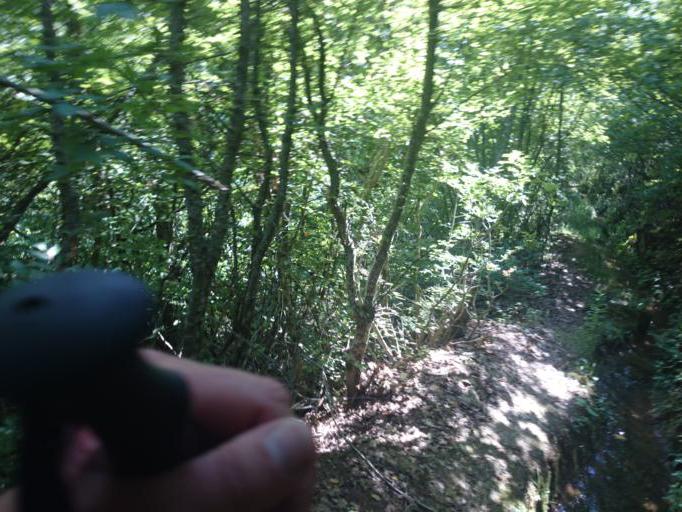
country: AL
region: Diber
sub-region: Rrethi i Dibres
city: Melan
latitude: 41.6201
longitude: 20.4239
